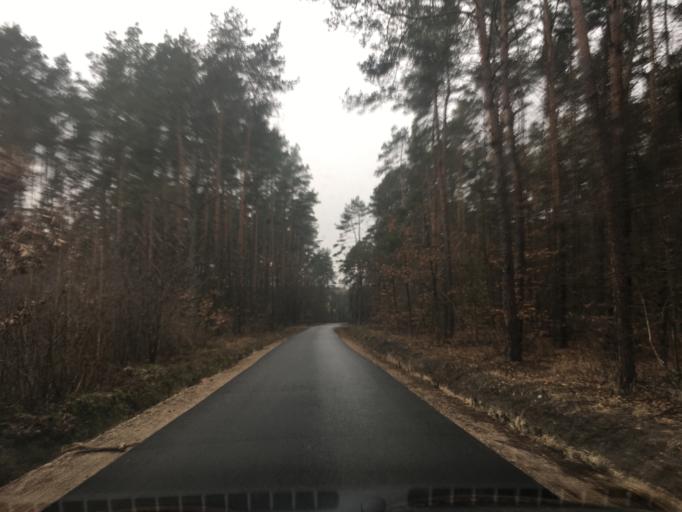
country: PL
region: Masovian Voivodeship
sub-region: Powiat piaseczynski
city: Lesznowola
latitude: 52.0793
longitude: 20.9268
